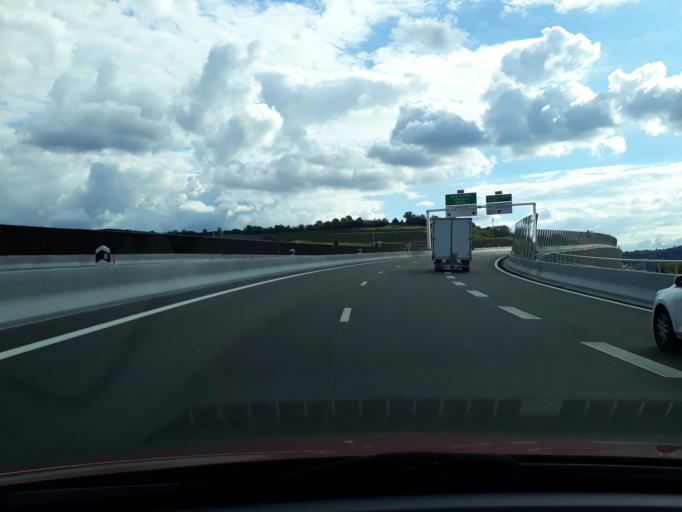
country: FR
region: Auvergne
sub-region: Departement de la Haute-Loire
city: Chadrac
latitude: 45.0522
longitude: 3.9066
